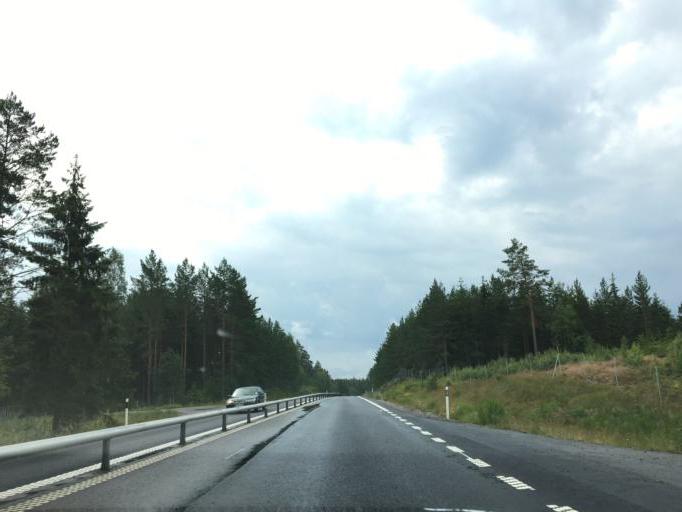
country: SE
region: Soedermanland
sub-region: Katrineholms Kommun
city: Katrineholm
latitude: 58.8961
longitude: 16.2088
